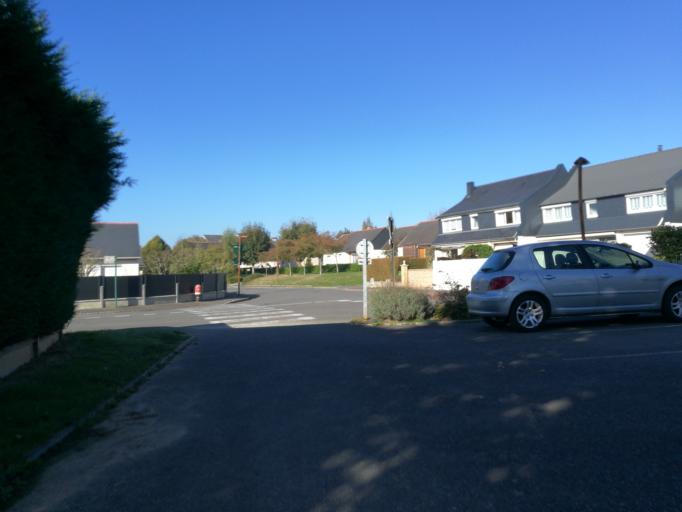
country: FR
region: Brittany
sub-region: Departement d'Ille-et-Vilaine
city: Bedee
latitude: 48.1773
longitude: -1.9407
